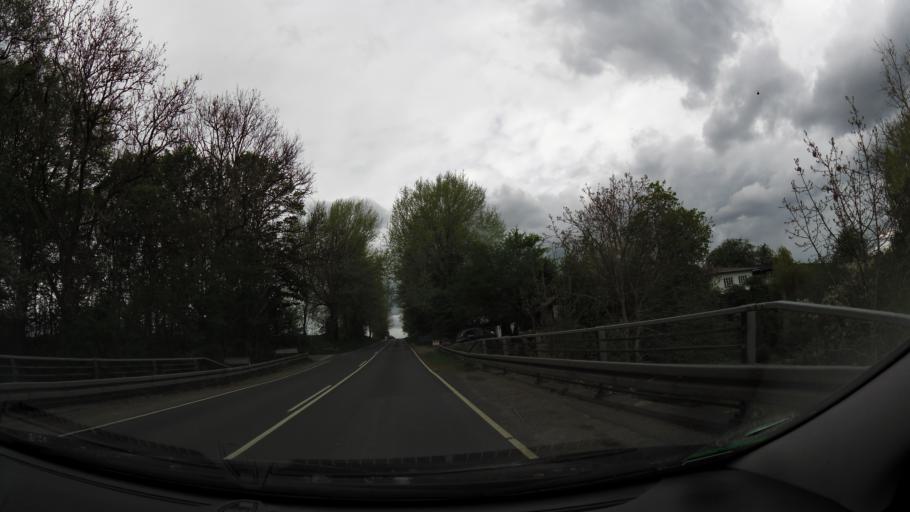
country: DK
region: South Denmark
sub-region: Svendborg Kommune
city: Thuro By
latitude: 55.1726
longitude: 10.7340
